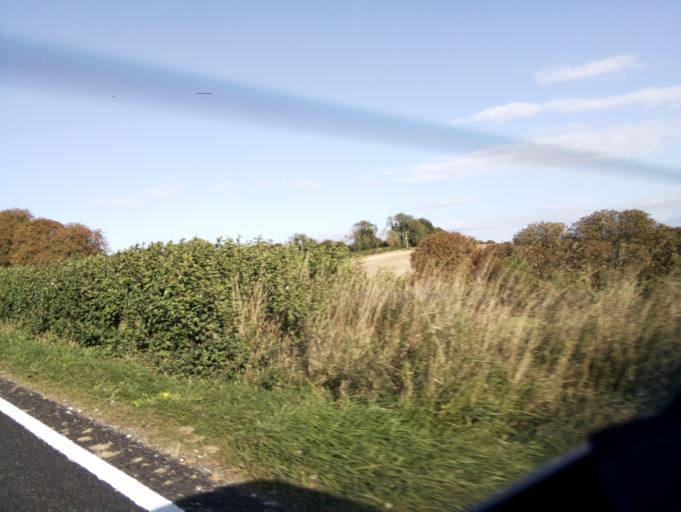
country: GB
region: England
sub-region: Hampshire
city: Four Marks
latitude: 51.0186
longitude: -1.0822
